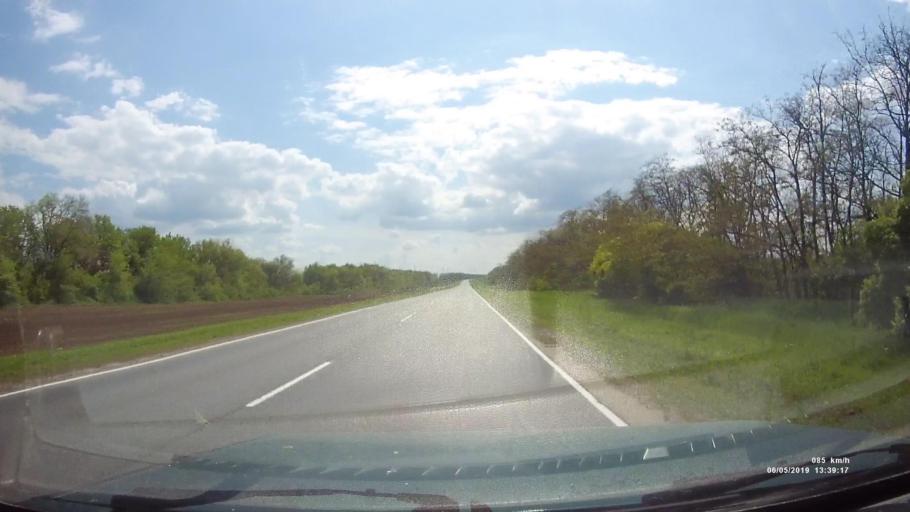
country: RU
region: Rostov
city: Ust'-Donetskiy
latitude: 47.6778
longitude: 40.7041
